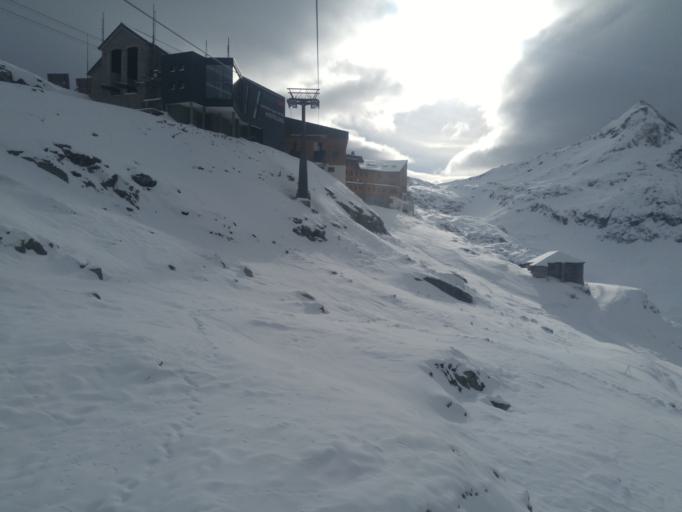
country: AT
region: Salzburg
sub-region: Politischer Bezirk Zell am See
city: Niedernsill
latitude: 47.1365
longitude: 12.6255
